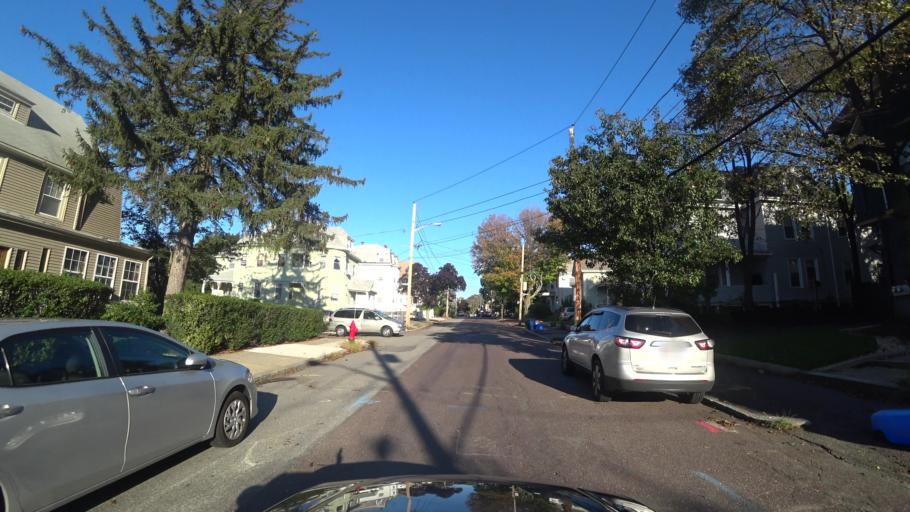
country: US
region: Massachusetts
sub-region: Middlesex County
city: Malden
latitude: 42.4169
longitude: -71.0676
